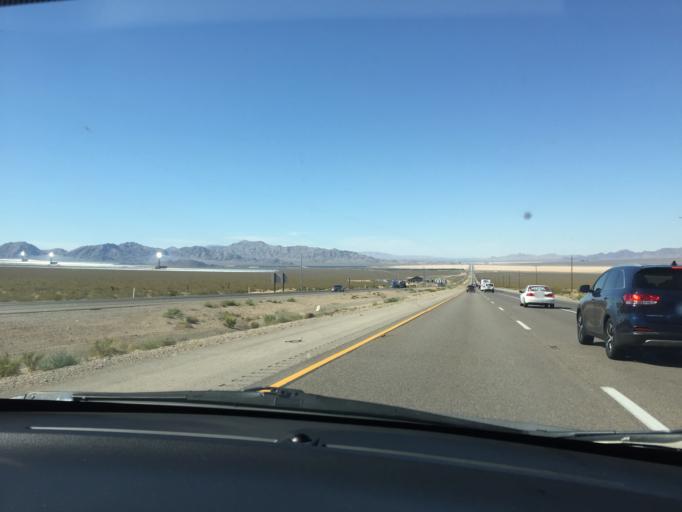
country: US
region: Nevada
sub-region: Clark County
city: Sandy Valley
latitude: 35.4898
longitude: -115.4414
